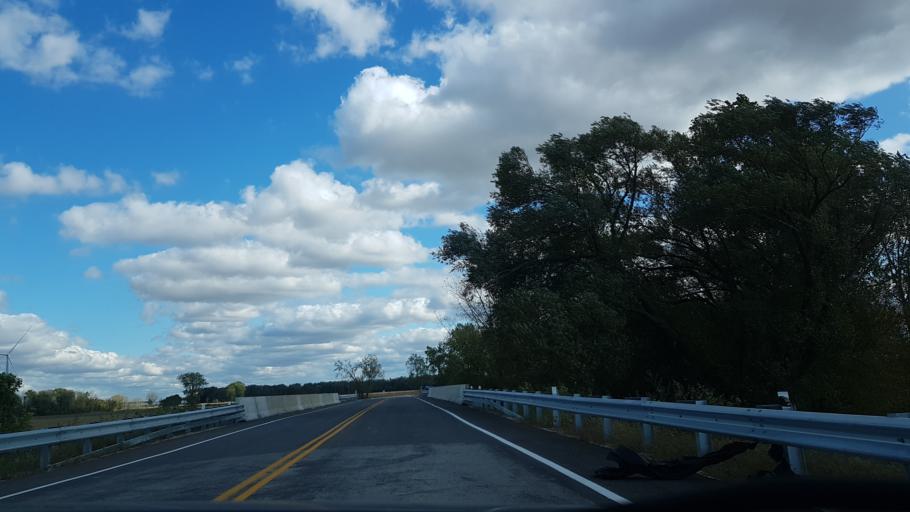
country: CA
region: Ontario
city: Lambton Shores
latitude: 43.2376
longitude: -81.7746
